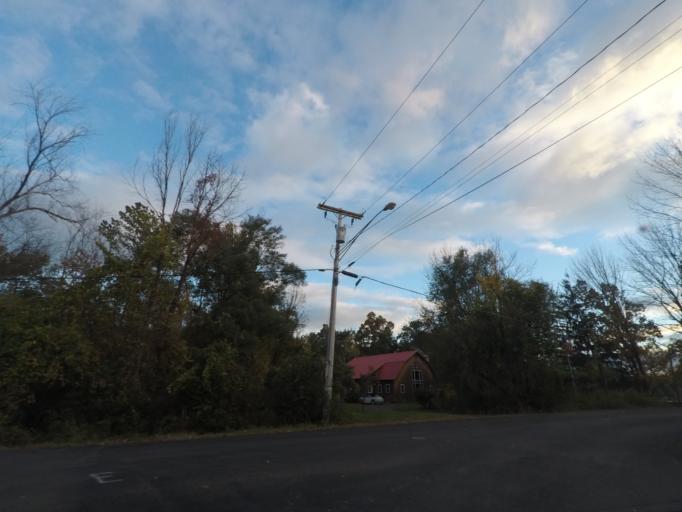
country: US
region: New York
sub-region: Rensselaer County
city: Nassau
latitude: 42.5359
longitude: -73.5750
